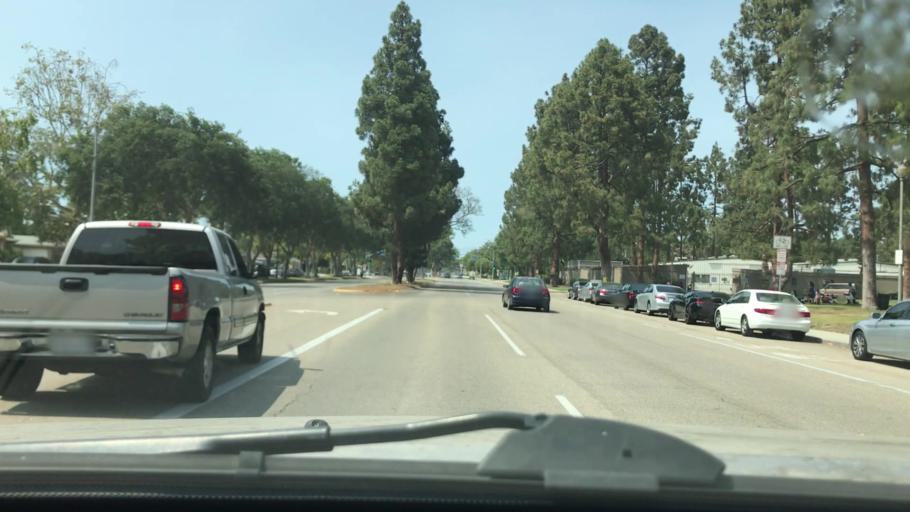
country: US
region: California
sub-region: Orange County
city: Rossmoor
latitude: 33.8048
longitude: -118.0992
